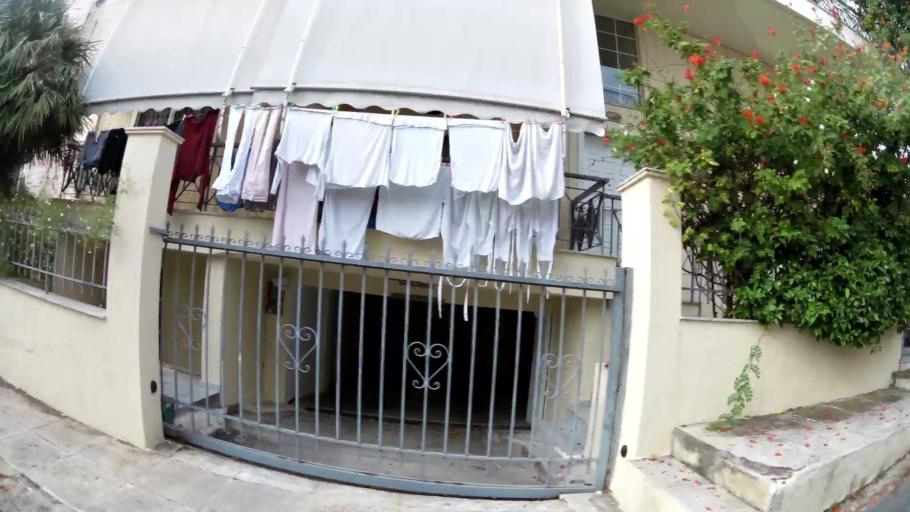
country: GR
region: Attica
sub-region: Nomarchia Athinas
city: Kamateron
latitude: 38.0589
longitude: 23.7024
